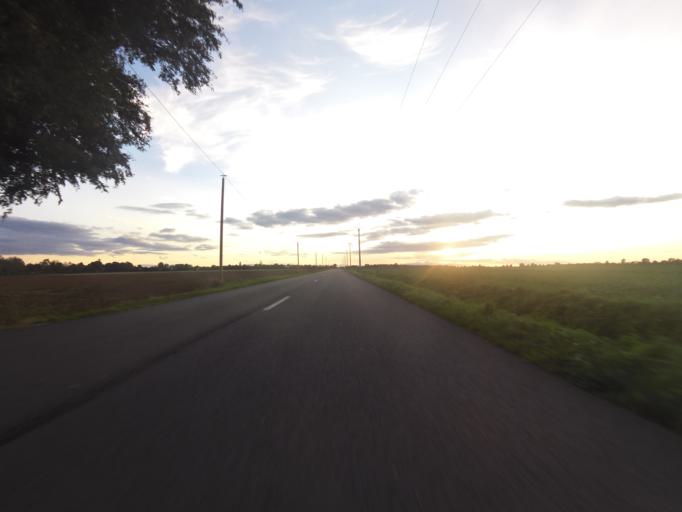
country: FR
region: Lower Normandy
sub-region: Departement du Calvados
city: La Vespiere
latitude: 48.9713
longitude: 0.3179
